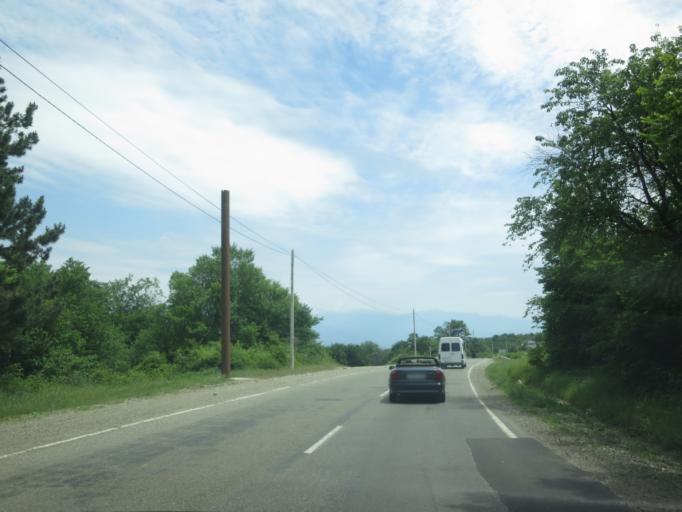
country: GE
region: Kakheti
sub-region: Telavi
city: Telavi
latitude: 41.9278
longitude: 45.4173
